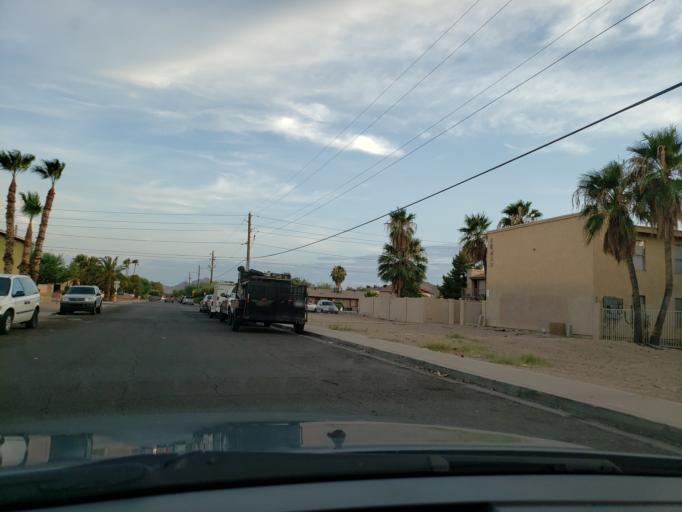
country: US
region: Arizona
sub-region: Maricopa County
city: Paradise Valley
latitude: 33.6342
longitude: -112.0157
